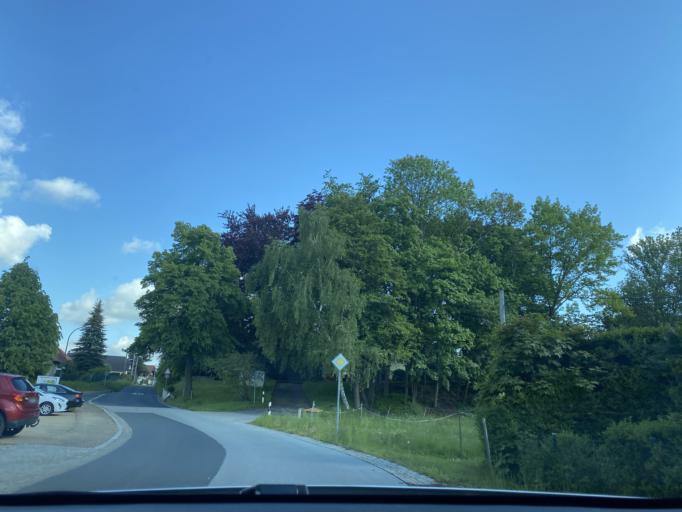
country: DE
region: Saxony
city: Markersdorf
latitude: 51.1398
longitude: 14.9254
